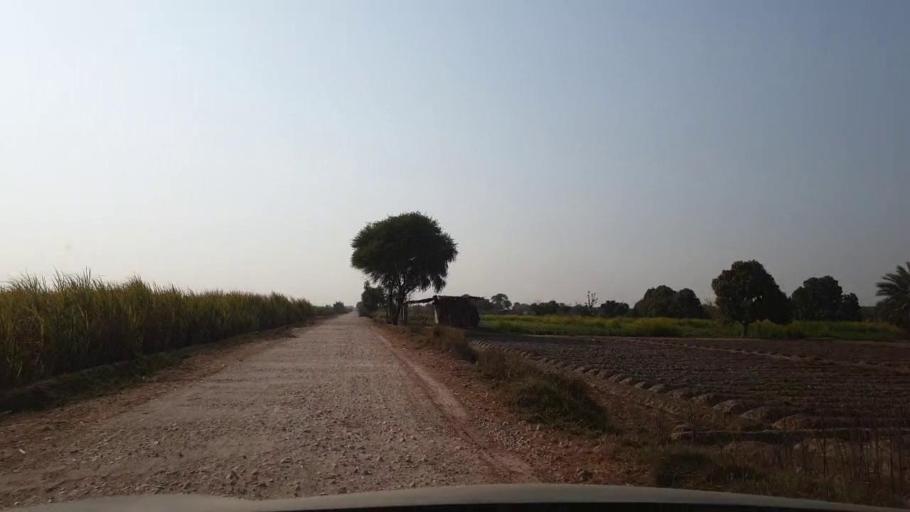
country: PK
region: Sindh
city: Tando Allahyar
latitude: 25.5818
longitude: 68.7879
